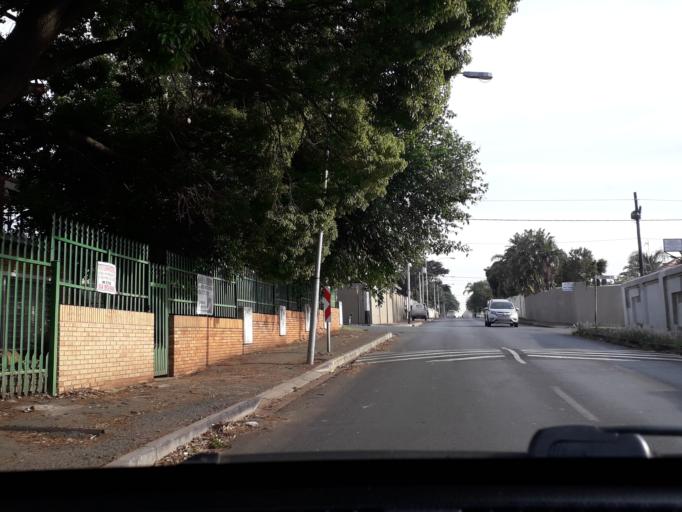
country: ZA
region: Gauteng
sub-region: City of Johannesburg Metropolitan Municipality
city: Johannesburg
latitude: -26.1576
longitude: 28.0956
